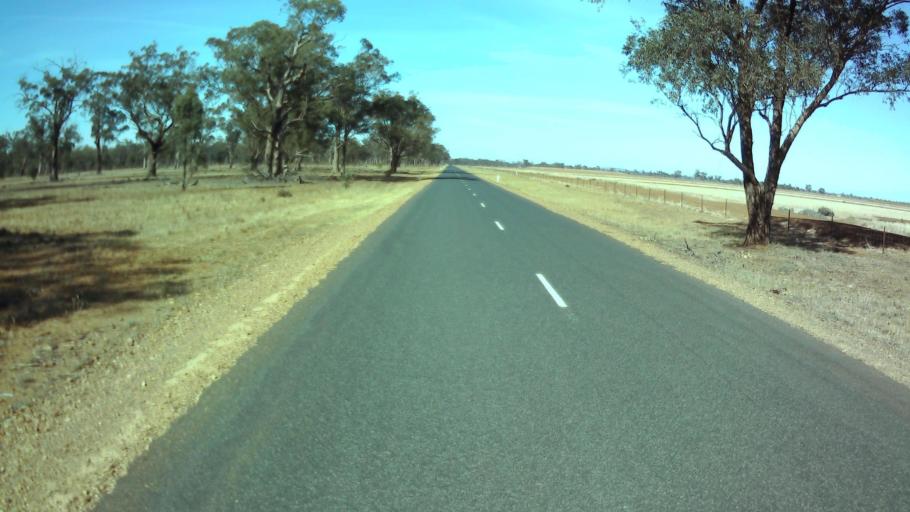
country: AU
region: New South Wales
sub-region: Weddin
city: Grenfell
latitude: -34.1198
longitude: 147.8130
